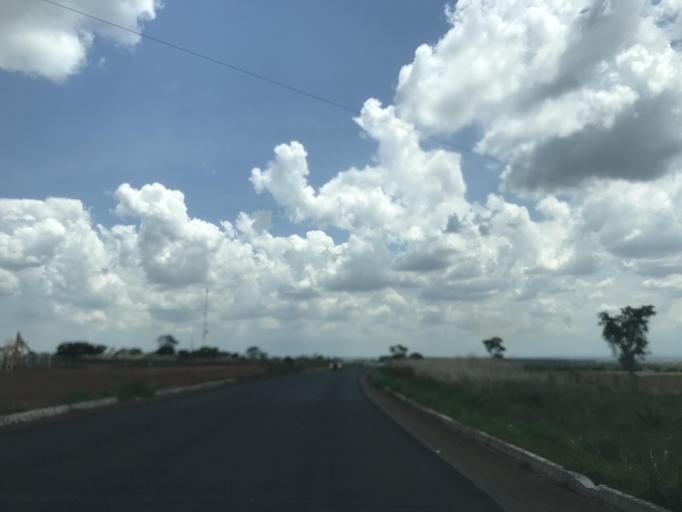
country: BR
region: Goias
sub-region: Piracanjuba
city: Piracanjuba
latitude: -17.3431
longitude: -48.7928
